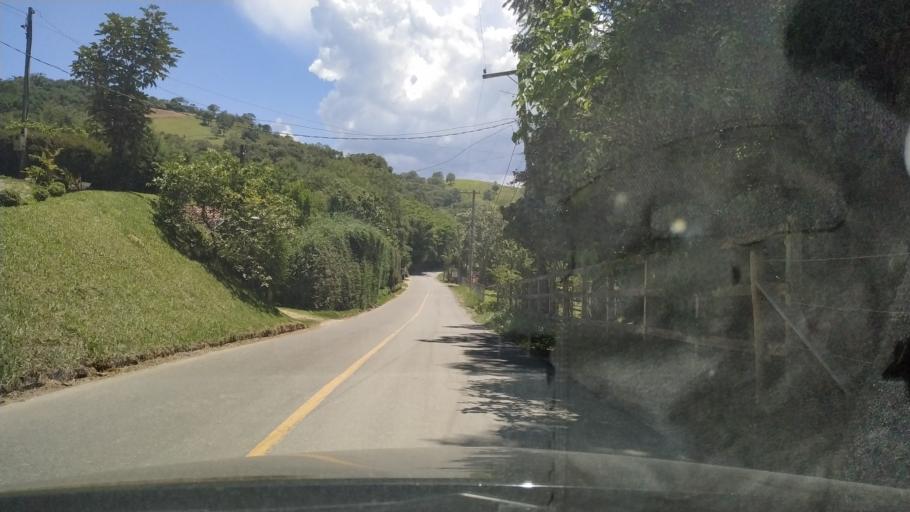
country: BR
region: Sao Paulo
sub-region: Campos Do Jordao
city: Campos do Jordao
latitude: -22.8011
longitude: -45.6978
